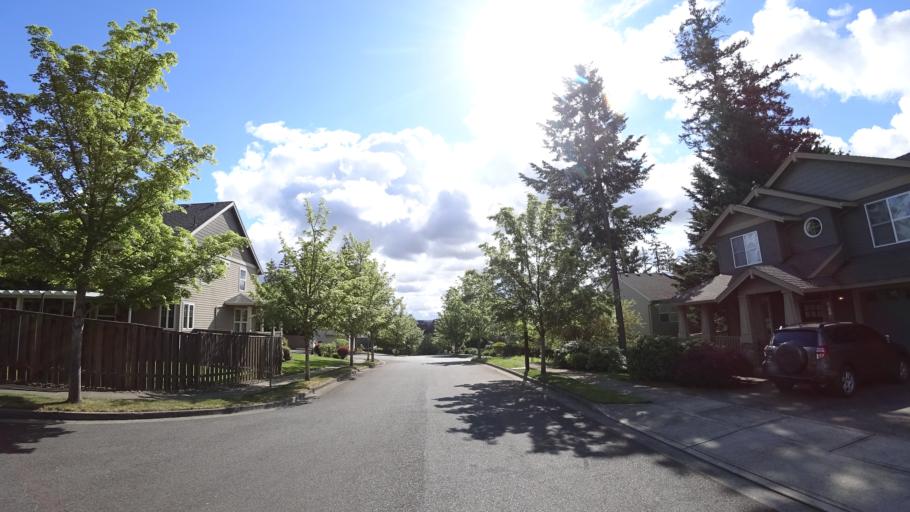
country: US
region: Oregon
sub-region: Washington County
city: Aloha
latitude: 45.4695
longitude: -122.8387
